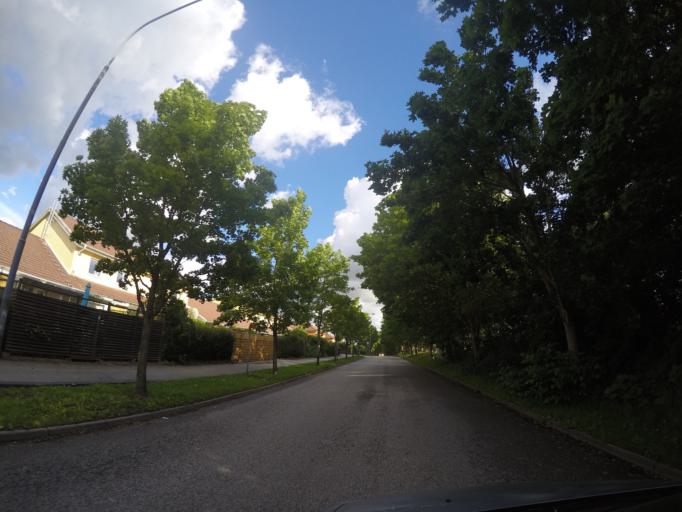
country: SE
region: Skane
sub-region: Lunds Kommun
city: Lund
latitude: 55.7001
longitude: 13.2457
